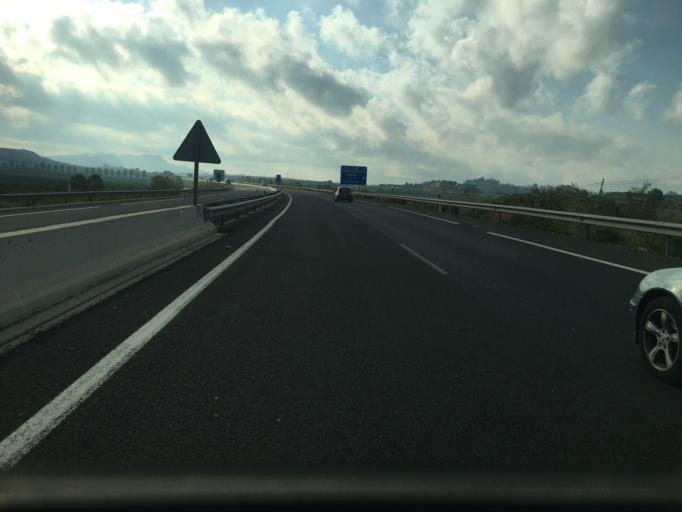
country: ES
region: Murcia
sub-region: Murcia
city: Beniel
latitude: 37.9960
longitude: -1.0032
